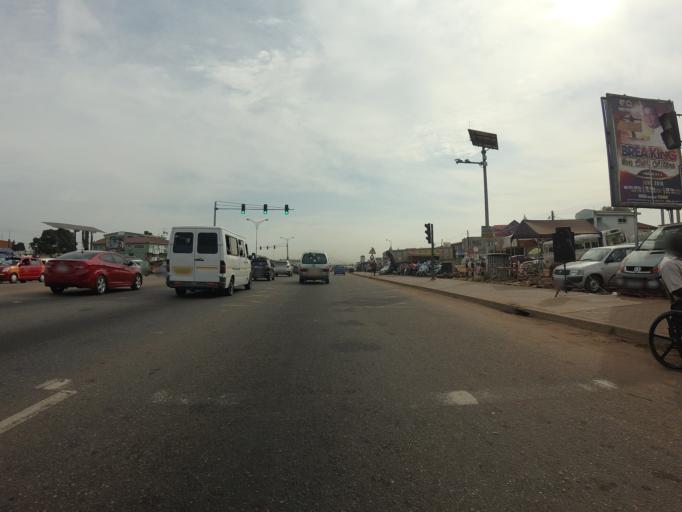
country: GH
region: Greater Accra
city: Dome
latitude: 5.6031
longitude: -0.2576
